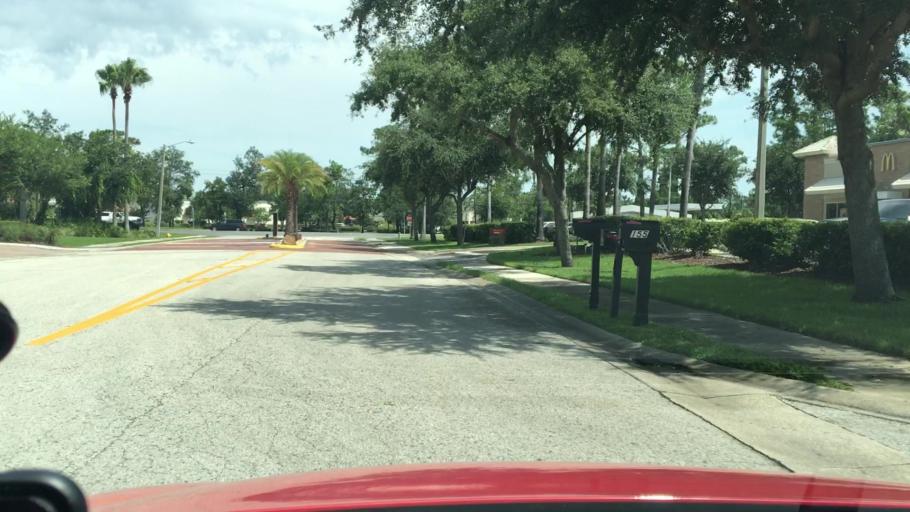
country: US
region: Florida
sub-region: Volusia County
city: Ormond Beach
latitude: 29.2552
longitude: -81.1183
